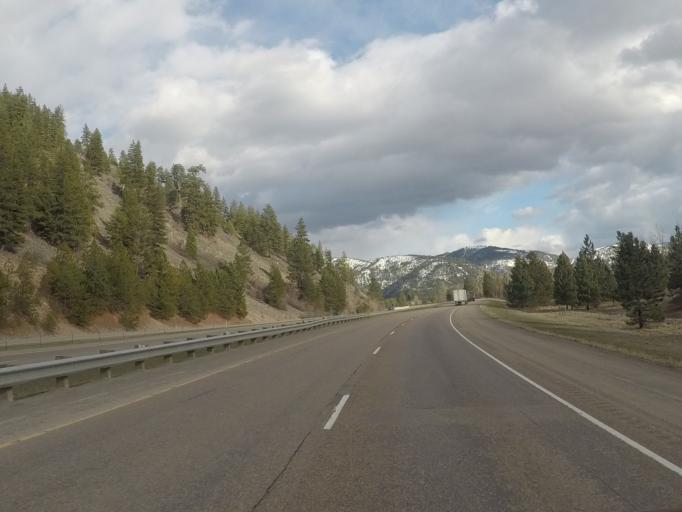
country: US
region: Montana
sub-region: Missoula County
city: Clinton
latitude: 46.7946
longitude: -113.7431
